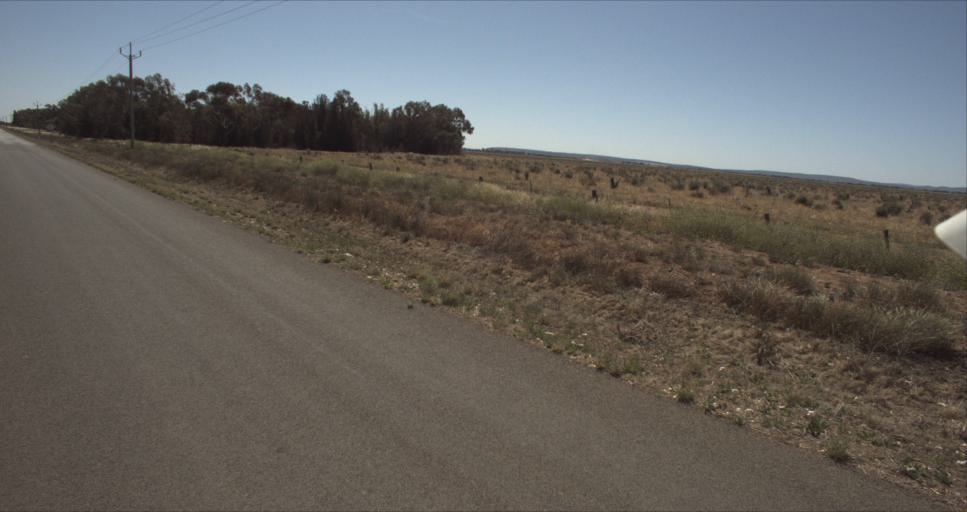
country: AU
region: New South Wales
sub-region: Leeton
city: Leeton
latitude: -34.4727
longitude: 146.2921
